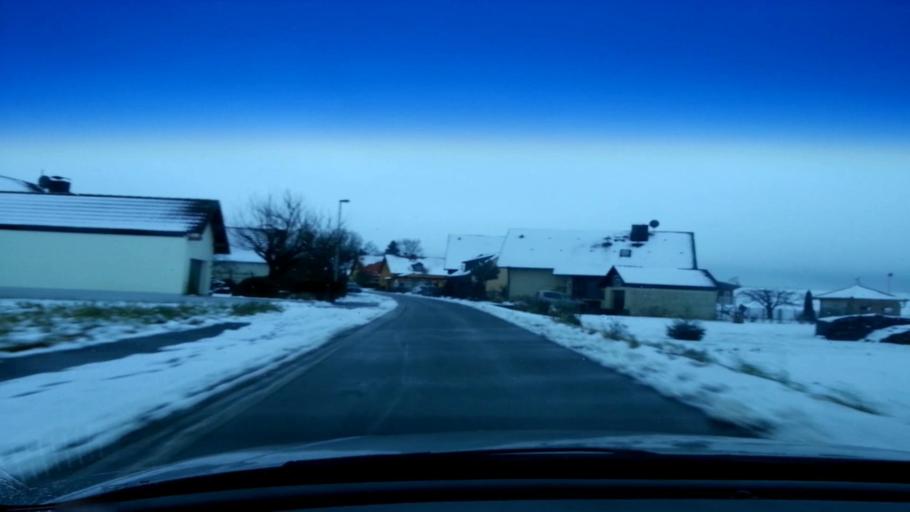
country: DE
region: Bavaria
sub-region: Upper Franconia
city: Schesslitz
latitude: 49.9593
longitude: 10.9947
